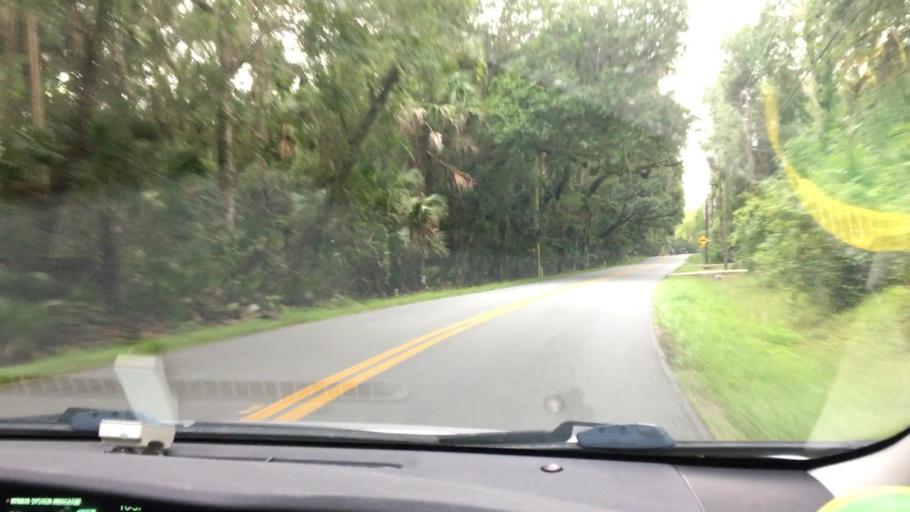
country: US
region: Florida
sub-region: Volusia County
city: Deltona
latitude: 28.8569
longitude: -81.2219
